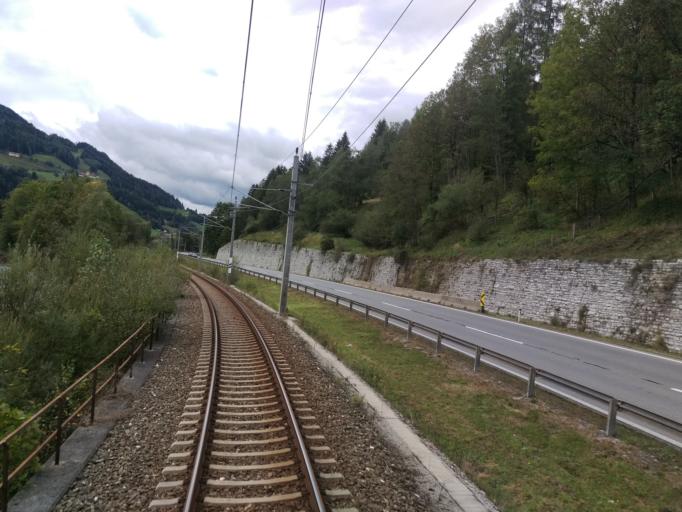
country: AT
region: Styria
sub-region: Politischer Bezirk Liezen
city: Schladming
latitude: 47.3892
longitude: 13.6330
